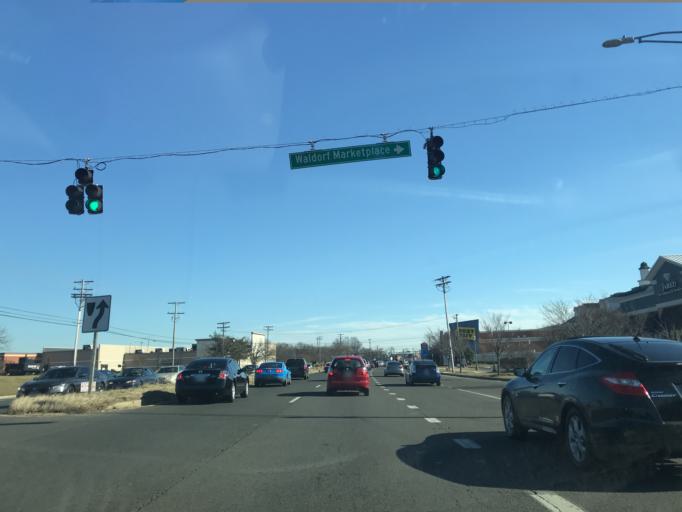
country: US
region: Maryland
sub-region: Charles County
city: Waldorf
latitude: 38.6282
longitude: -76.9140
